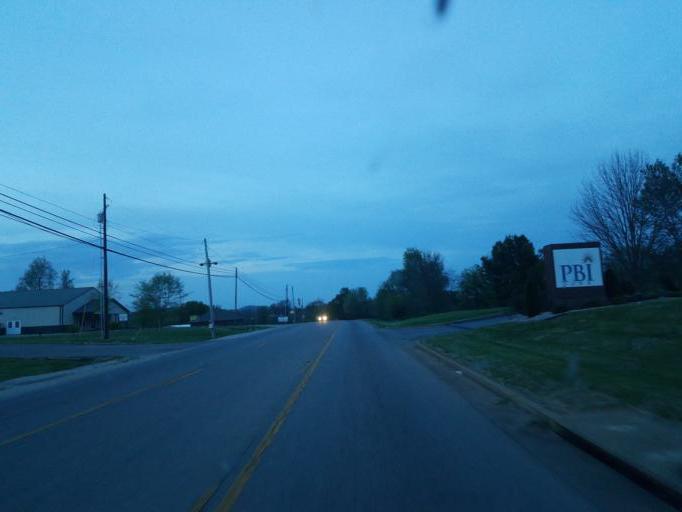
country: US
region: Kentucky
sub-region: Hart County
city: Munfordville
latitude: 37.2614
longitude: -85.8823
